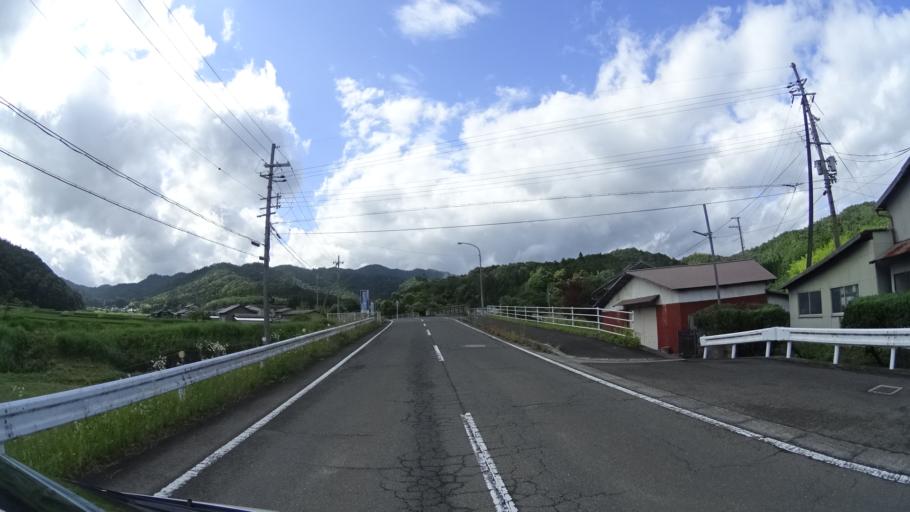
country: JP
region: Kyoto
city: Ayabe
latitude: 35.3727
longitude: 135.2396
